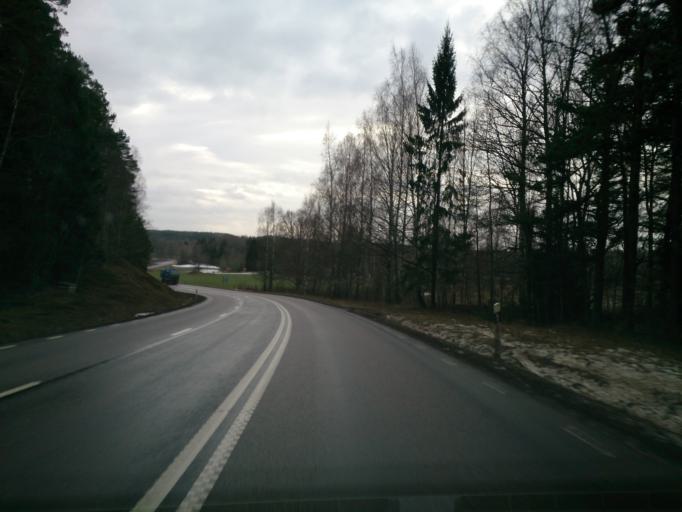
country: SE
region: OEstergoetland
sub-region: Atvidabergs Kommun
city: Atvidaberg
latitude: 58.2631
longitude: 15.9240
